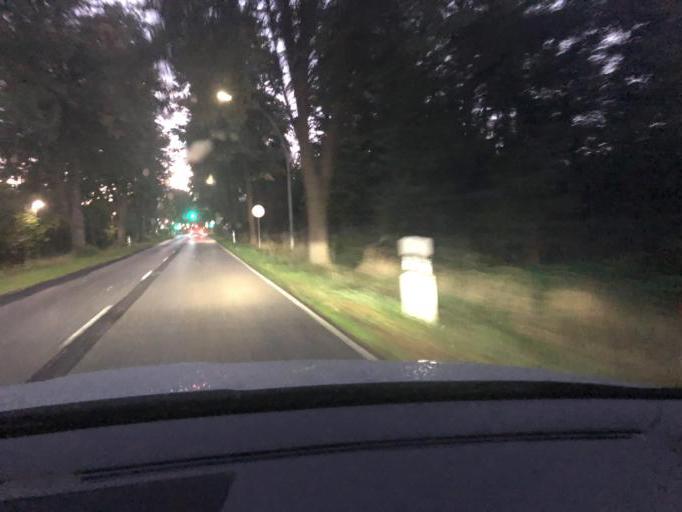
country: DE
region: Schleswig-Holstein
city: Gross Gronau
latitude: 53.8201
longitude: 10.7277
